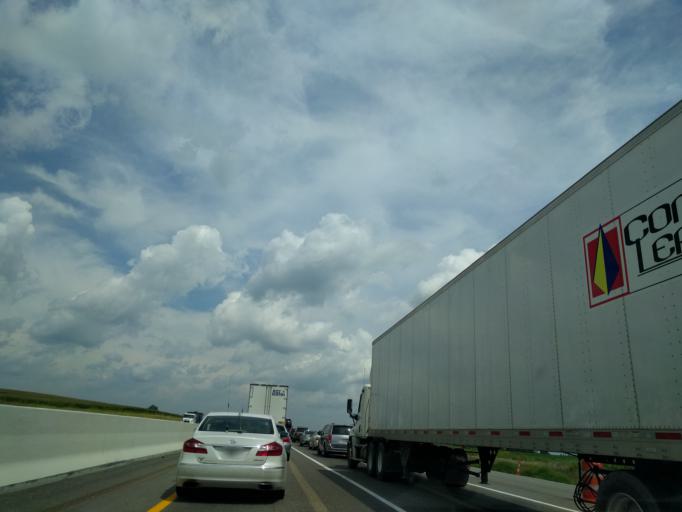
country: US
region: Kentucky
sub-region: Larue County
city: Hodgenville
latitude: 37.5476
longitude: -85.8795
